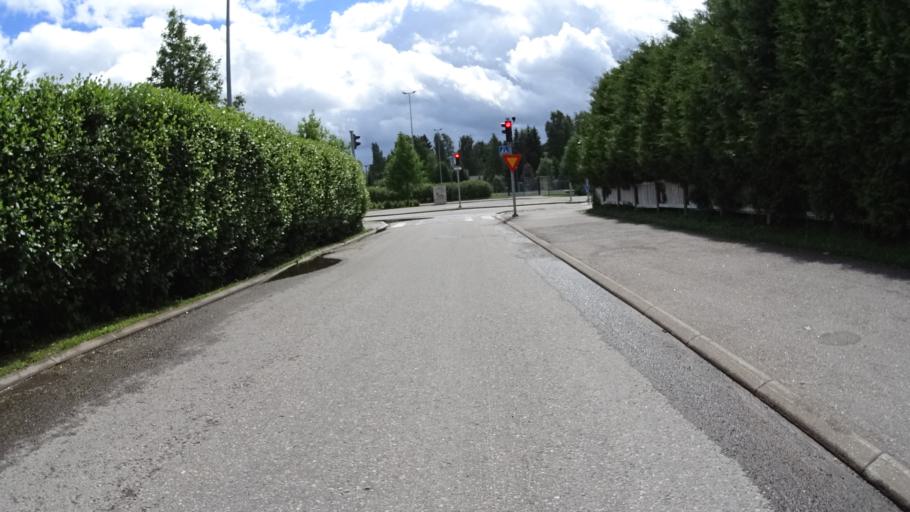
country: FI
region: Uusimaa
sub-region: Helsinki
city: Kilo
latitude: 60.2347
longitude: 24.8187
